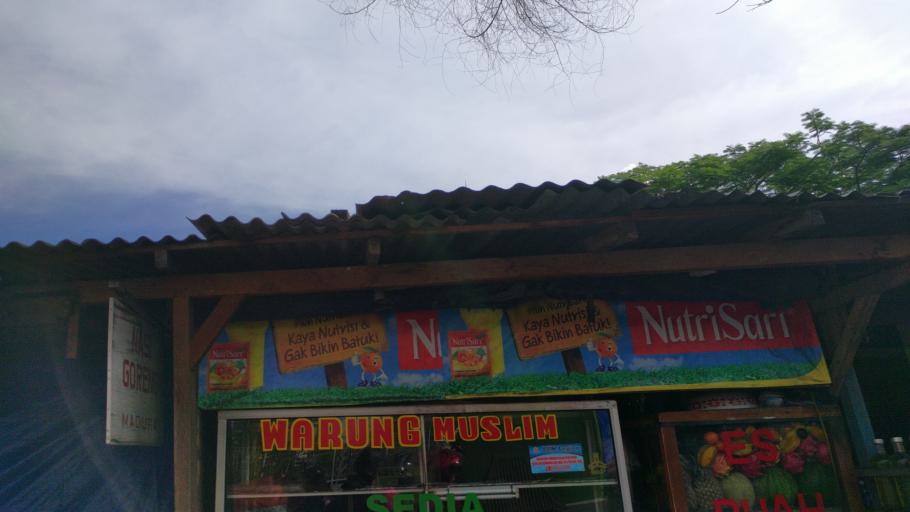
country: ID
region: Bali
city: Kuta
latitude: -8.6983
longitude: 115.1741
